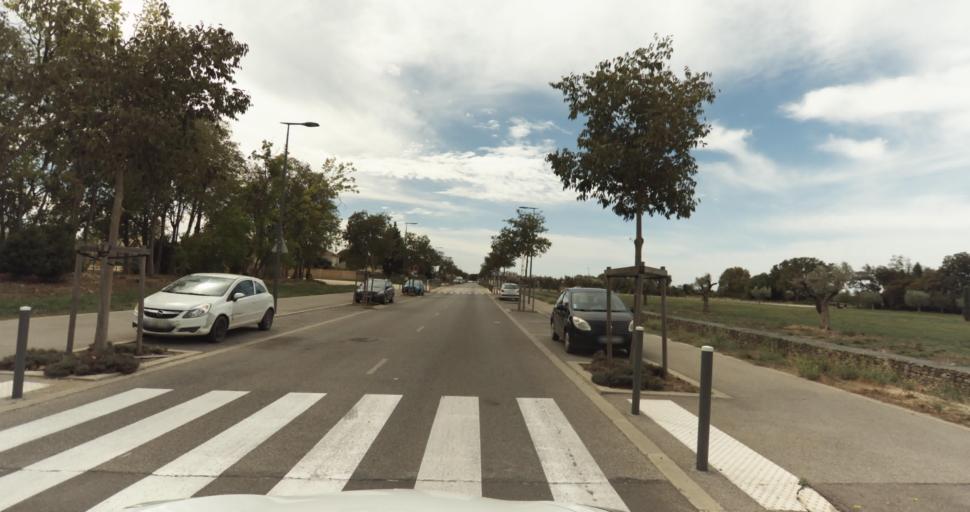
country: FR
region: Provence-Alpes-Cote d'Azur
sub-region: Departement des Bouches-du-Rhone
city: Miramas
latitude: 43.5924
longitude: 4.9939
